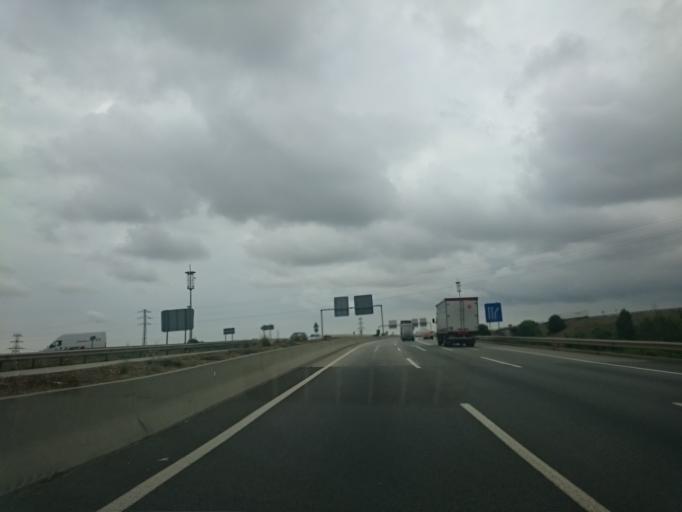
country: ES
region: Catalonia
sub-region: Provincia de Barcelona
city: Cornella de Llobregat
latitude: 41.3460
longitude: 2.0920
